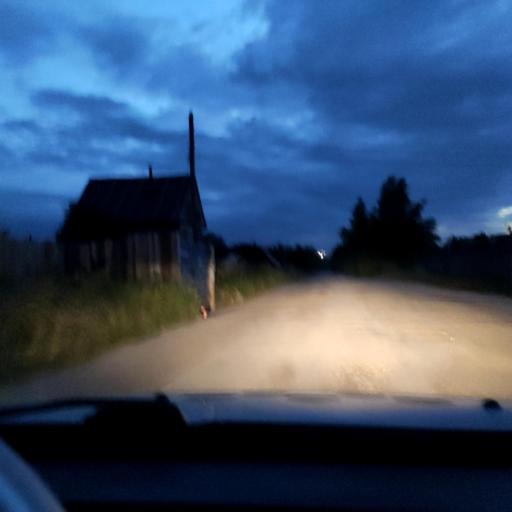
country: RU
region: Perm
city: Kondratovo
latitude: 58.0294
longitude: 56.0657
